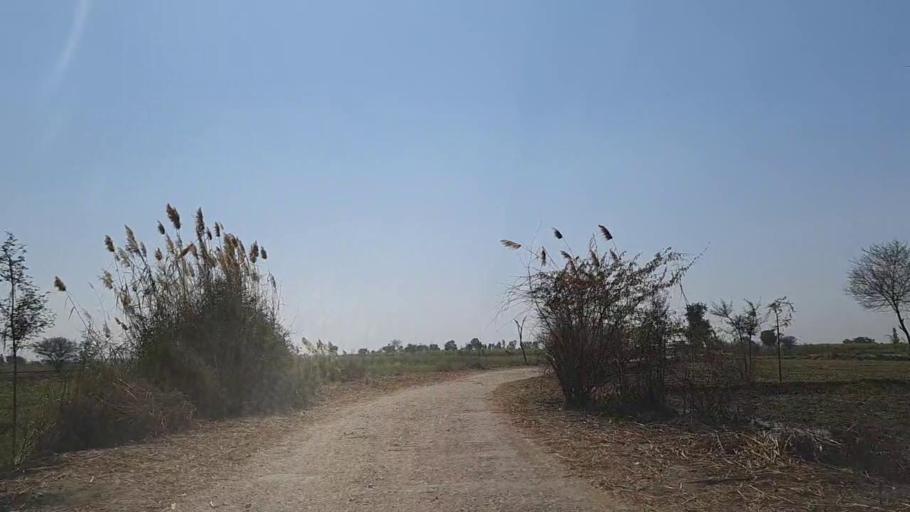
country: PK
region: Sindh
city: Samaro
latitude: 25.3722
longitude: 69.3276
